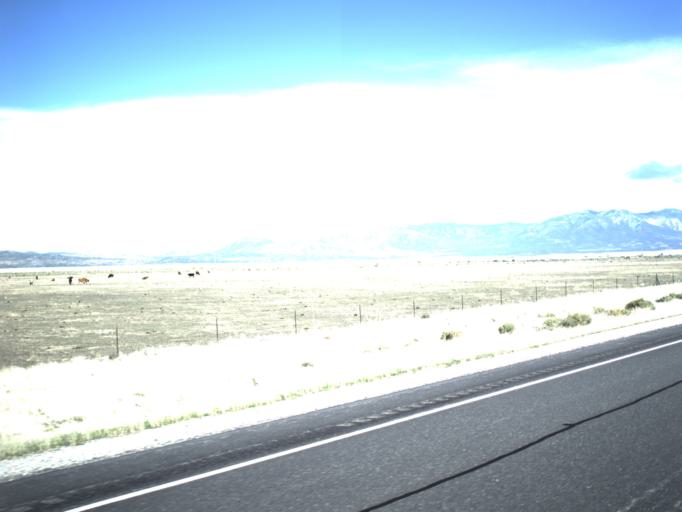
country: US
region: Utah
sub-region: Millard County
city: Fillmore
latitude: 39.1524
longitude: -112.4016
